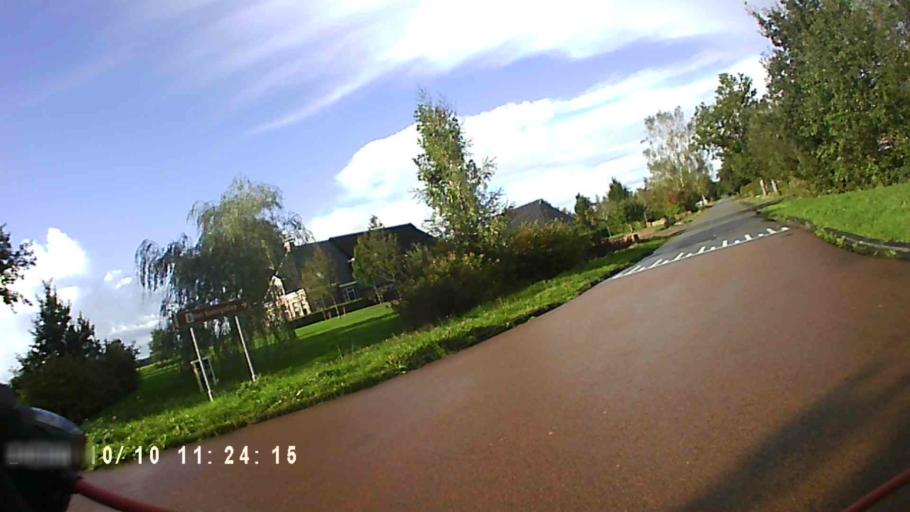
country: NL
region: Friesland
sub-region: Gemeente Smallingerland
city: Drachtstercompagnie
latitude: 53.0875
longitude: 6.1758
